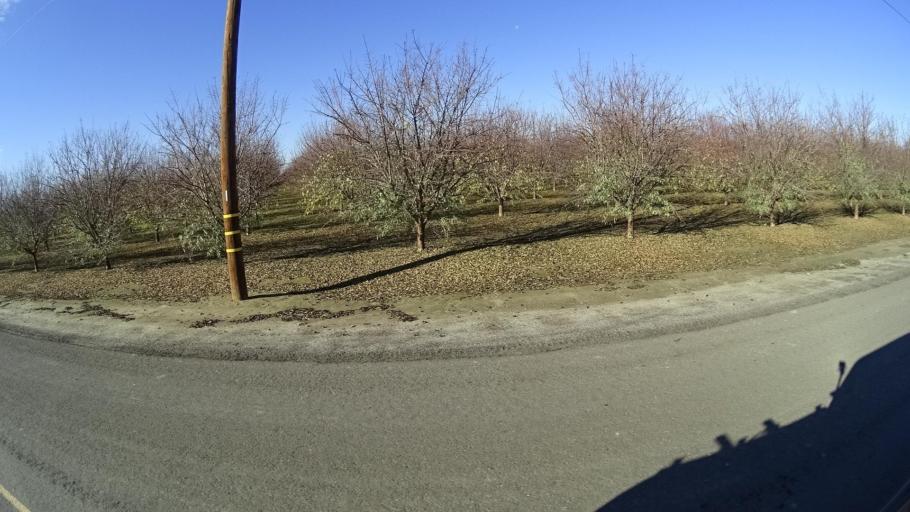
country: US
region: California
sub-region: Kern County
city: Delano
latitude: 35.7435
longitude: -119.3119
